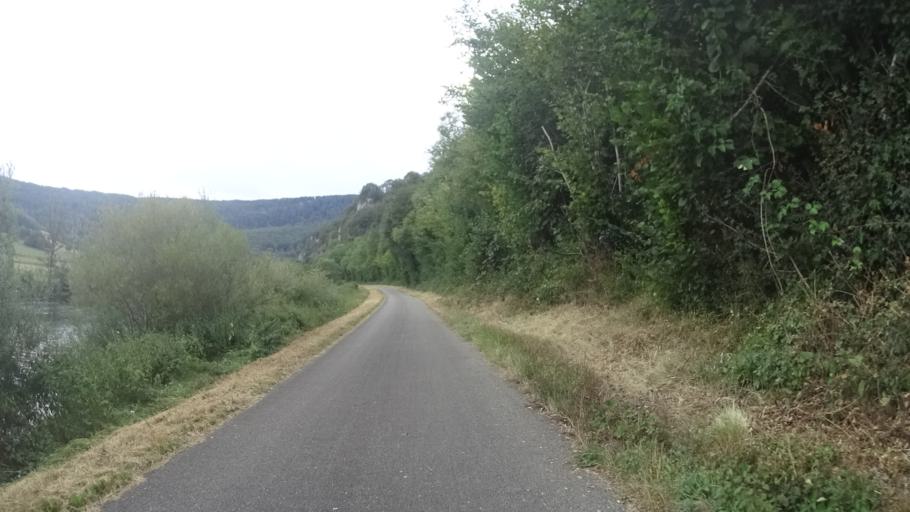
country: FR
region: Franche-Comte
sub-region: Departement du Doubs
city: Baume-les-Dames
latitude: 47.3400
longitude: 6.3164
